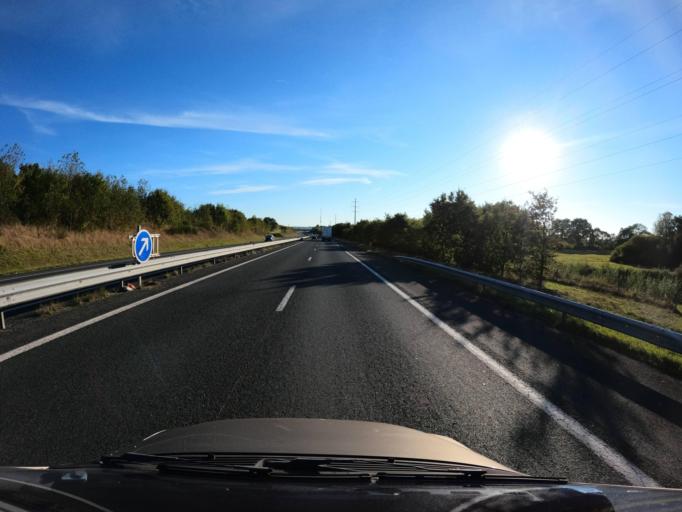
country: FR
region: Pays de la Loire
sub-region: Departement de Maine-et-Loire
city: Mazieres-en-Mauges
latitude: 47.0538
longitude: -0.8343
